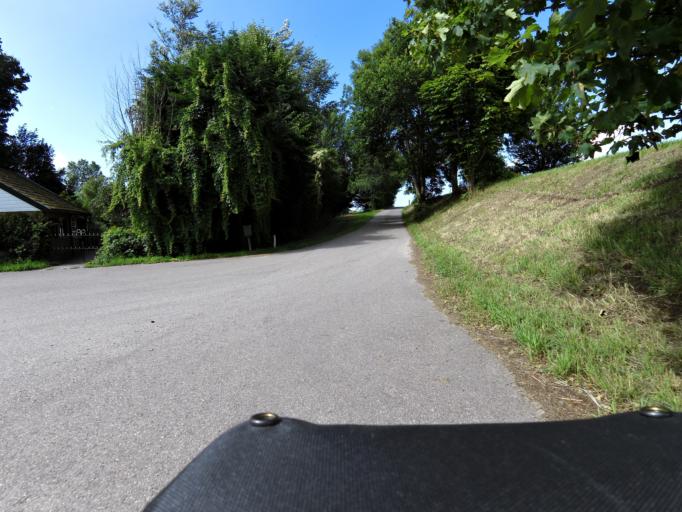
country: NL
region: South Holland
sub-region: Gemeente Goeree-Overflakkee
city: Dirksland
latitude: 51.7782
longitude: 4.0492
